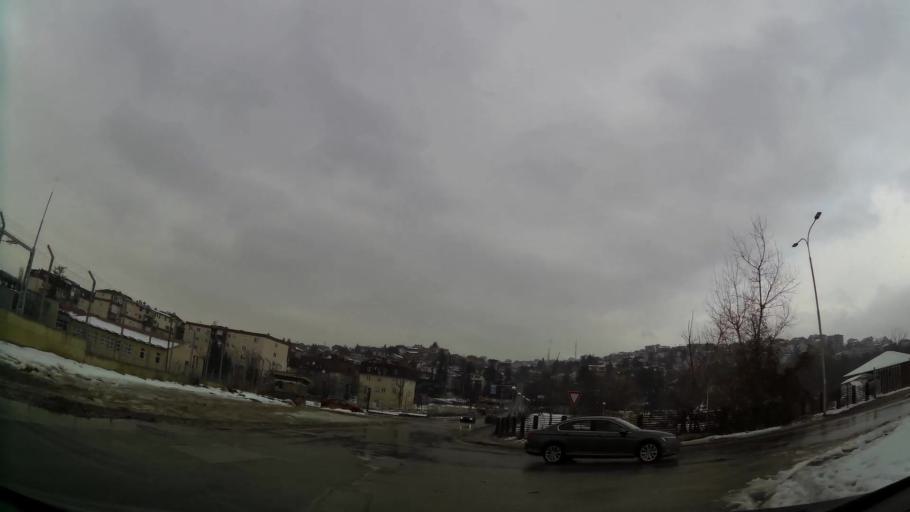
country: XK
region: Pristina
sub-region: Komuna e Prishtines
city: Pristina
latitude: 42.6648
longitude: 21.1770
